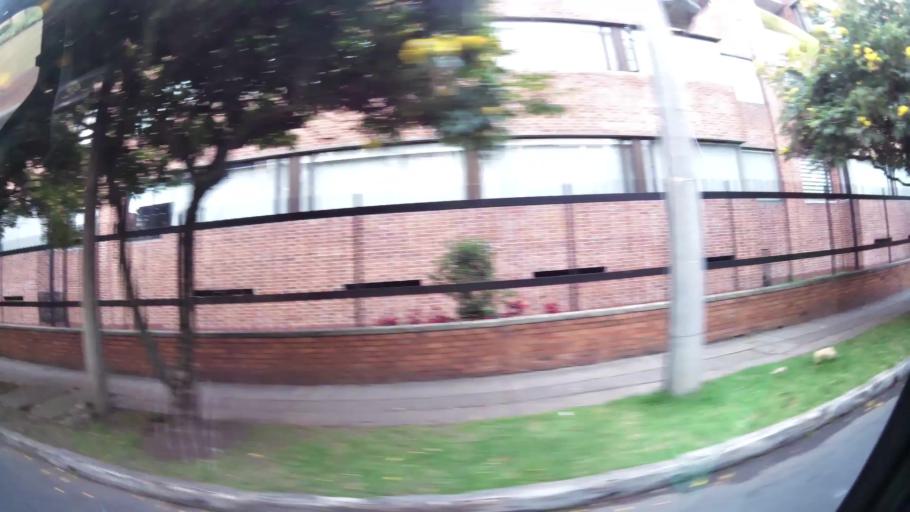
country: CO
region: Bogota D.C.
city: Barrio San Luis
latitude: 4.7007
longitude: -74.0359
